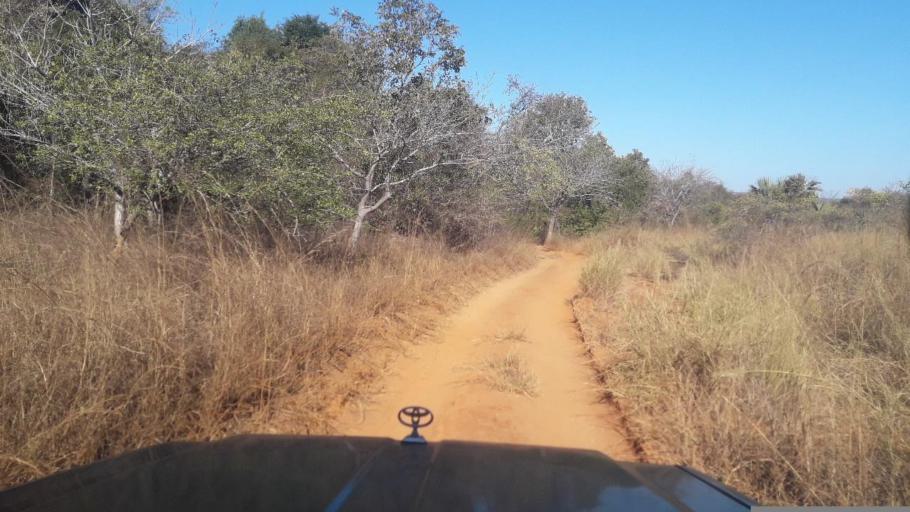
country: MG
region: Boeny
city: Sitampiky
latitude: -16.4175
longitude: 45.6110
